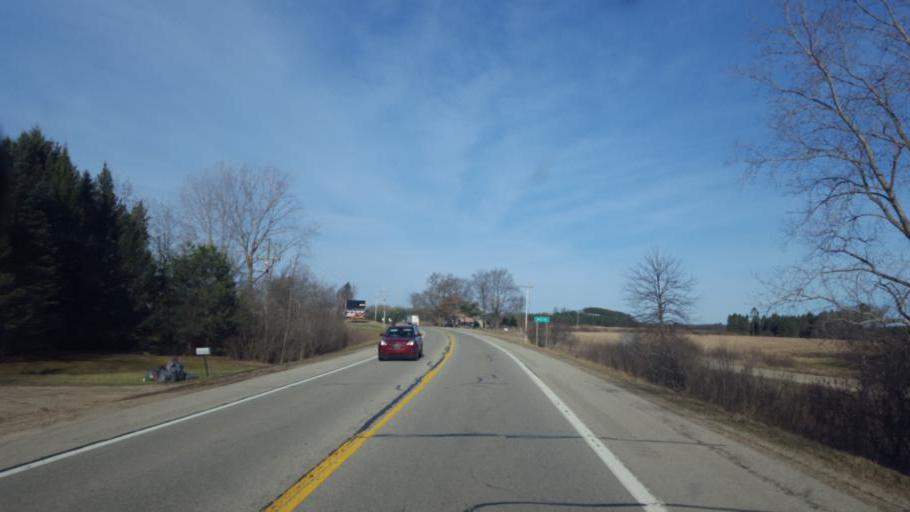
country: US
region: Michigan
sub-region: Montcalm County
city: Lakeview
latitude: 43.4296
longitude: -85.1599
